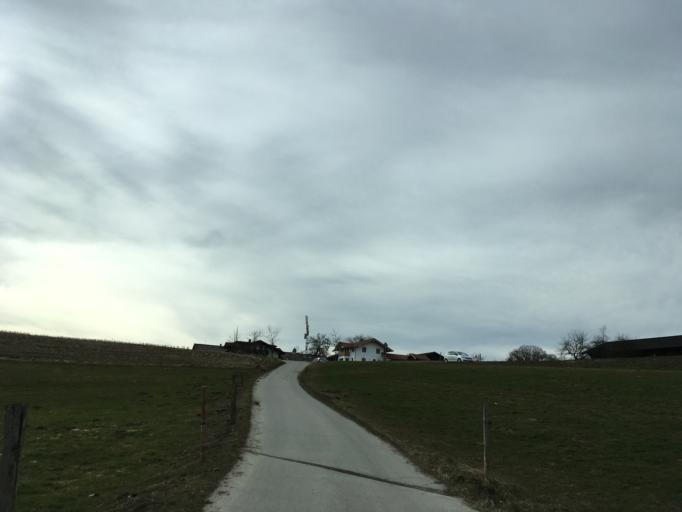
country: DE
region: Bavaria
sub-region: Upper Bavaria
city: Rimsting
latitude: 47.8895
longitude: 12.3665
